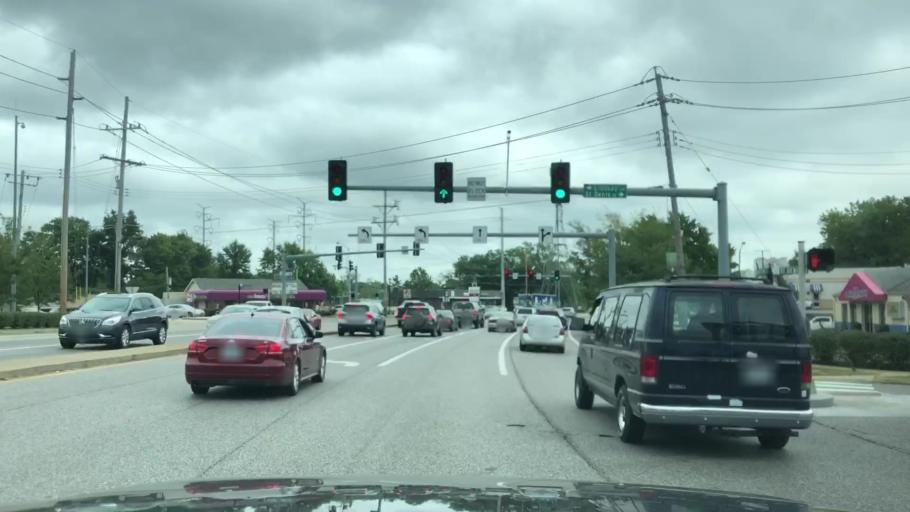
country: US
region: Missouri
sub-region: Saint Louis County
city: Florissant
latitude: 38.7999
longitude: -90.3348
